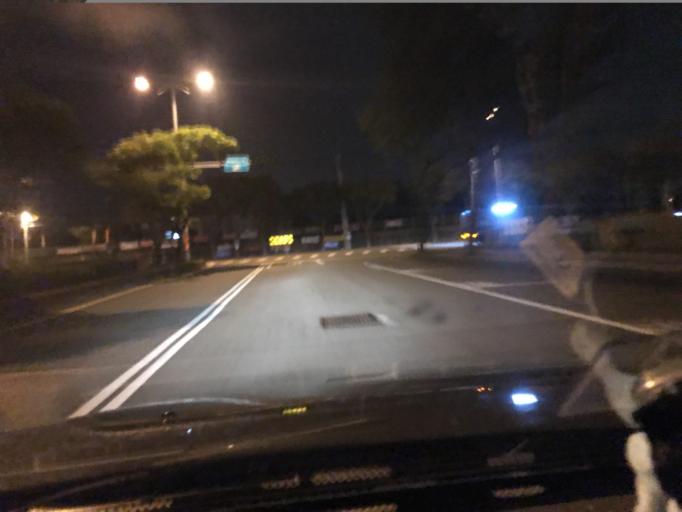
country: TW
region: Taiwan
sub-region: Hsinchu
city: Zhubei
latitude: 24.8031
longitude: 121.0452
